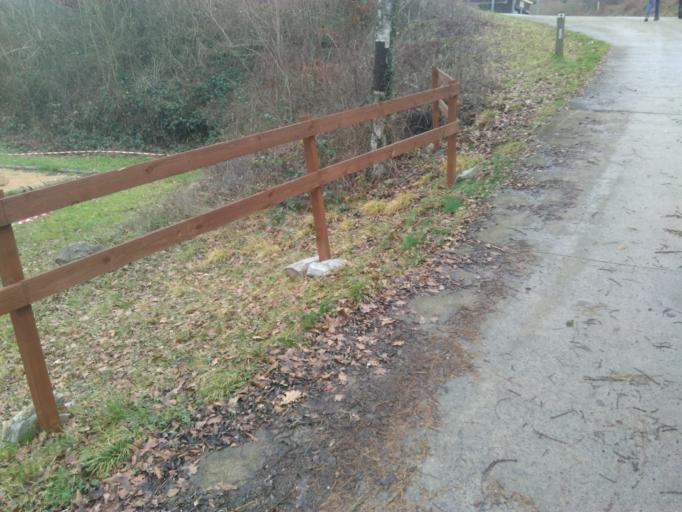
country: BE
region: Wallonia
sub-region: Province de Namur
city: Houyet
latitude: 50.2111
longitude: 4.9641
